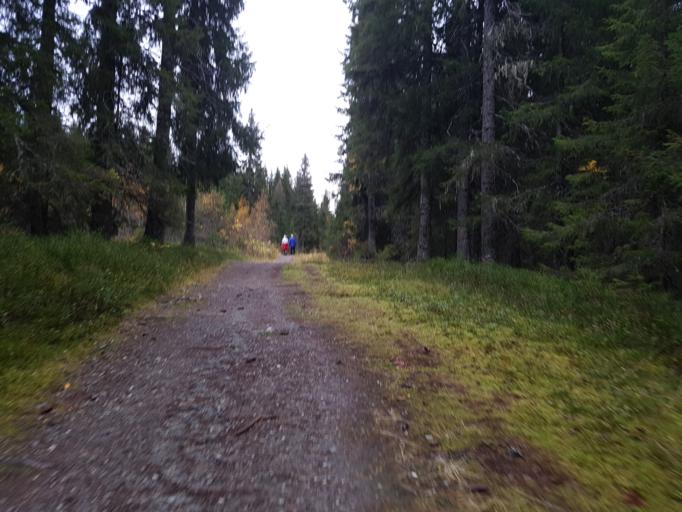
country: NO
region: Sor-Trondelag
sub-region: Melhus
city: Melhus
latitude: 63.3800
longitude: 10.2570
